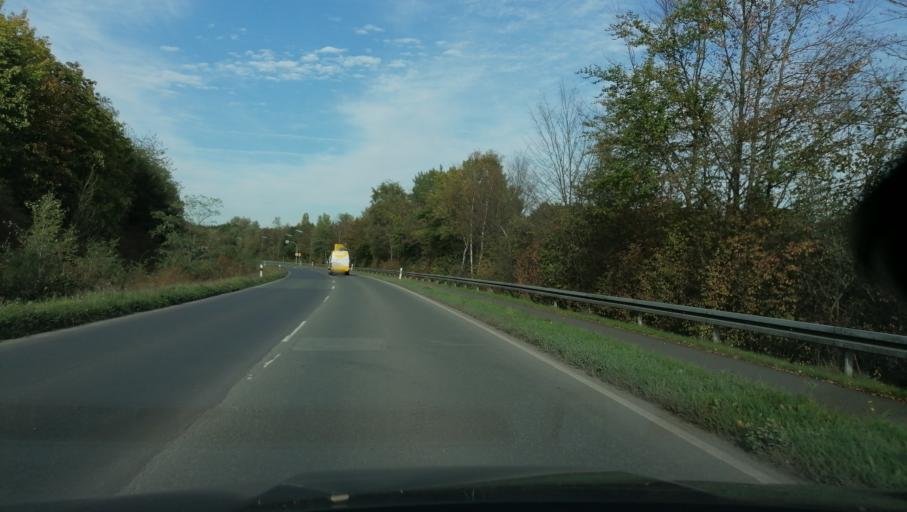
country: DE
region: North Rhine-Westphalia
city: Herten
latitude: 51.5670
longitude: 7.1758
